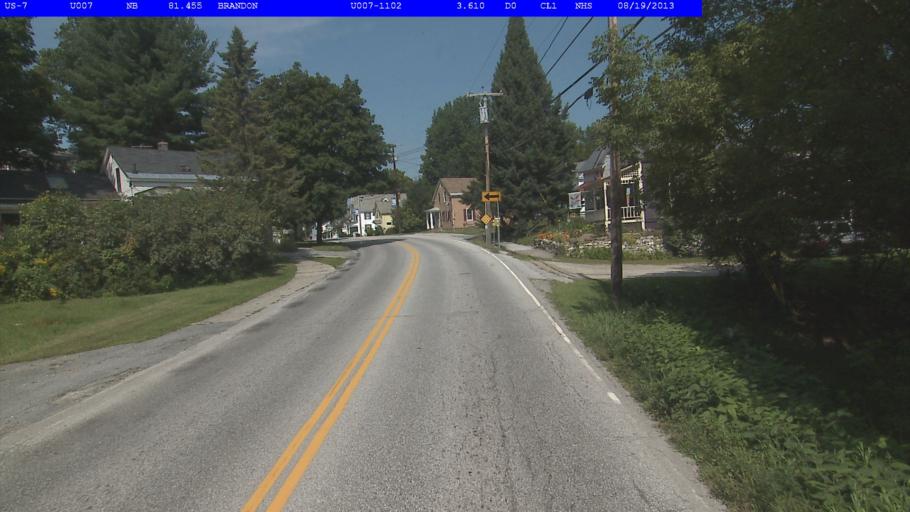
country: US
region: Vermont
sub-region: Rutland County
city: Brandon
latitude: 43.7961
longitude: -73.0819
